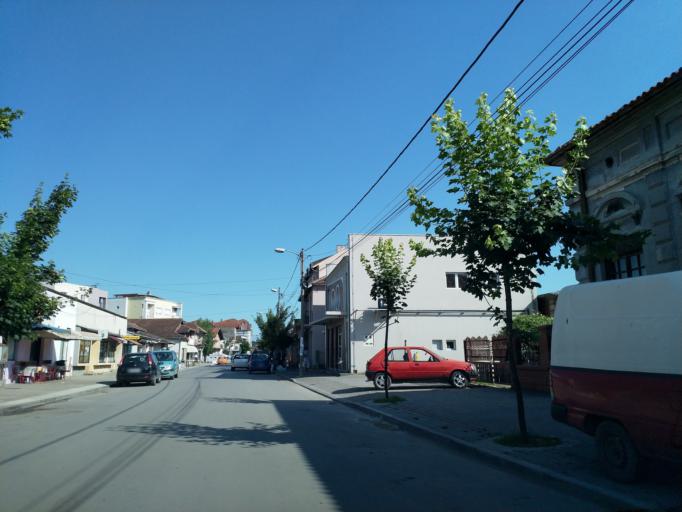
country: RS
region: Central Serbia
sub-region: Pomoravski Okrug
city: Paracin
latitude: 43.8577
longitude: 21.4099
